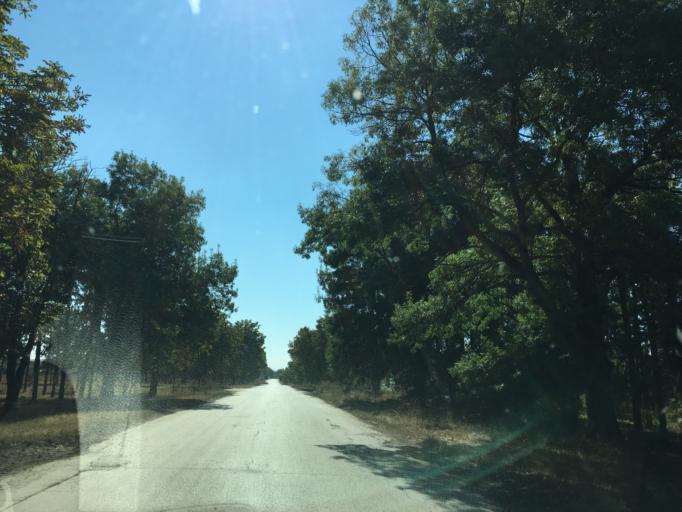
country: BG
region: Pleven
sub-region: Obshtina Knezha
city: Knezha
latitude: 43.5136
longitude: 24.0825
